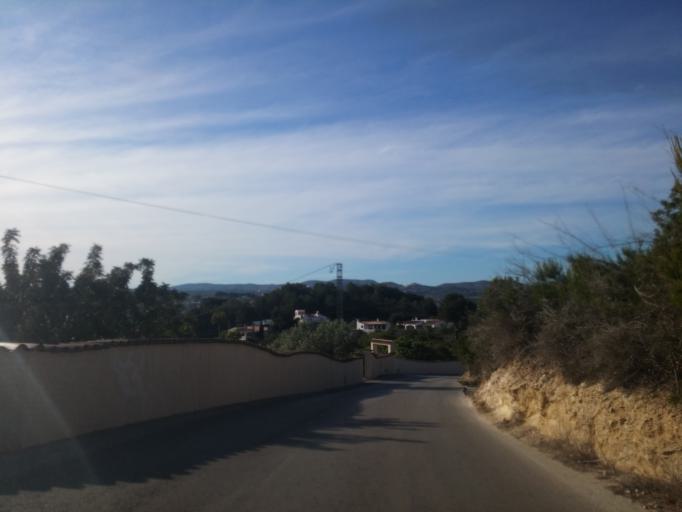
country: ES
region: Valencia
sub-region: Provincia de Alicante
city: Moraira
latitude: 38.6976
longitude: 0.1377
